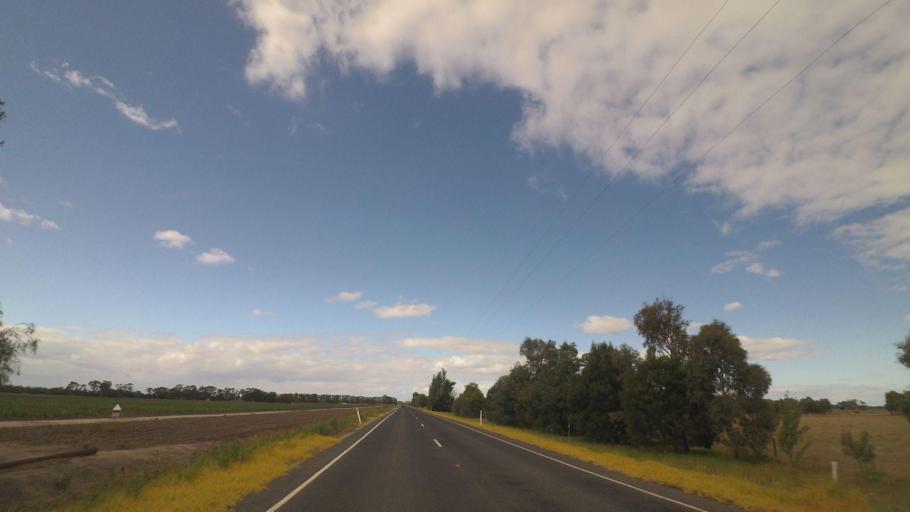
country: AU
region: Victoria
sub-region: Cardinia
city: Pakenham South
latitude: -38.1454
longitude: 145.5568
